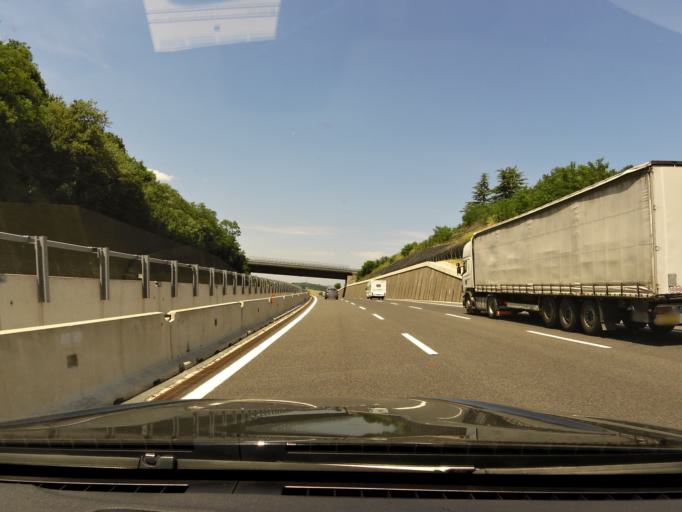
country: IT
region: The Marches
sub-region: Provincia di Pesaro e Urbino
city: Pesaro
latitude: 43.8692
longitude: 12.9239
